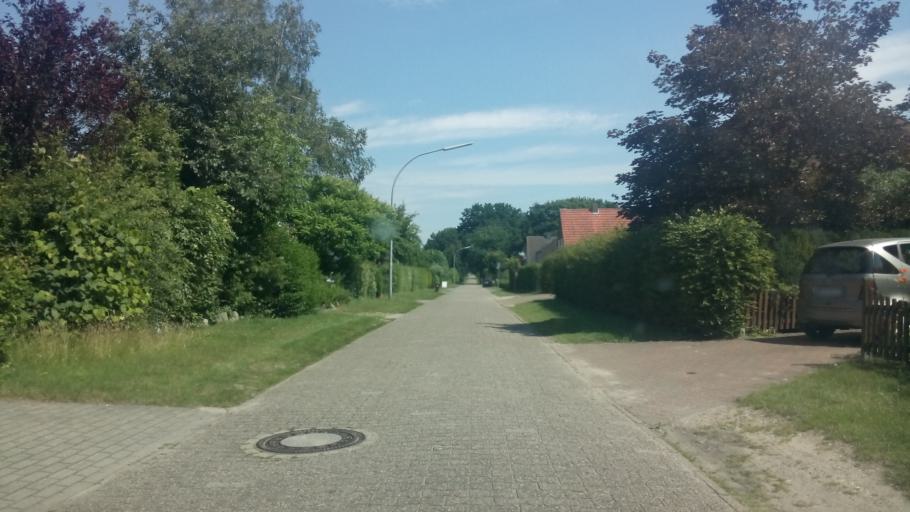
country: DE
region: Lower Saxony
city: Hambergen
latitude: 53.2721
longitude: 8.8231
